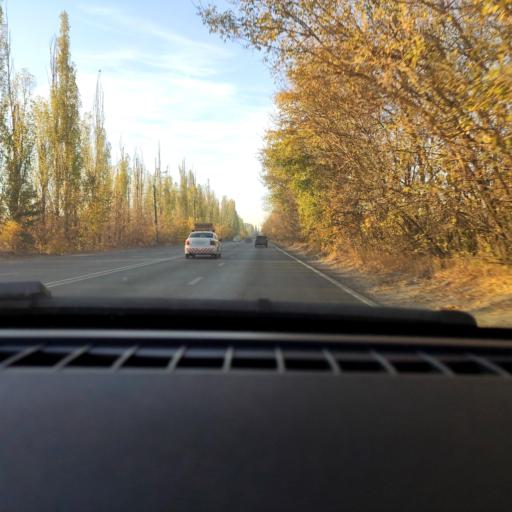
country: RU
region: Voronezj
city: Maslovka
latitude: 51.6102
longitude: 39.2565
